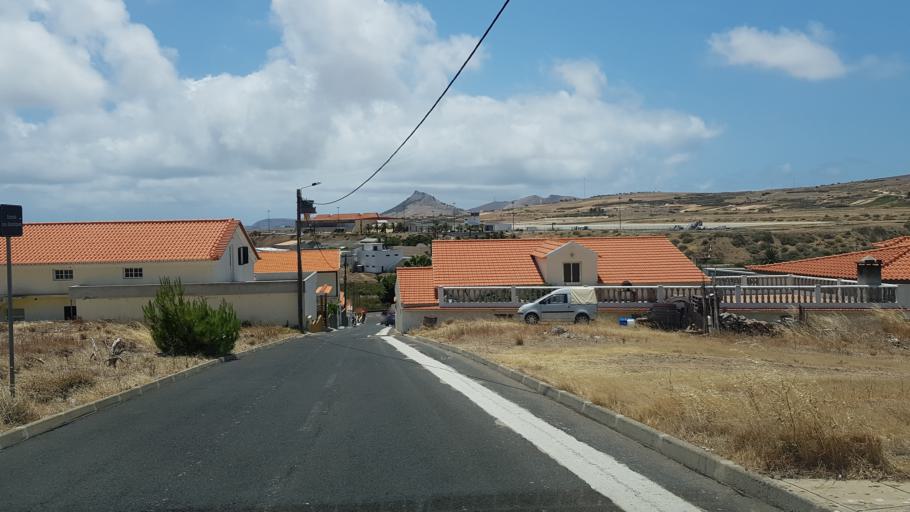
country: PT
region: Madeira
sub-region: Porto Santo
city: Camacha
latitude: 33.0750
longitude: -16.3419
